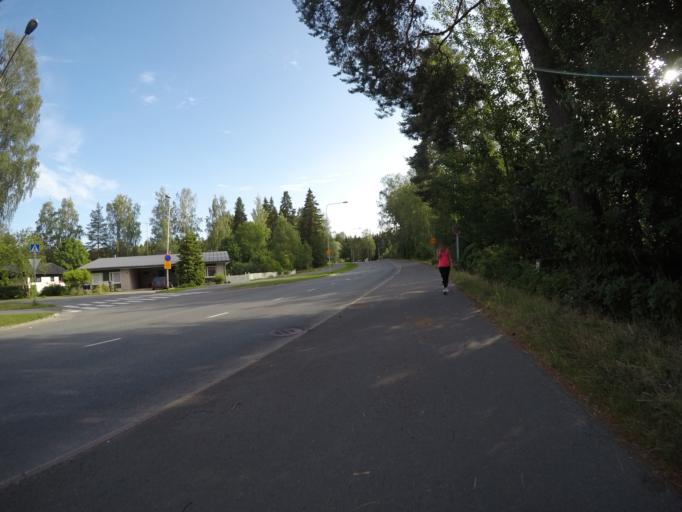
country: FI
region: Haeme
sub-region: Haemeenlinna
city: Haemeenlinna
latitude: 60.9745
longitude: 24.3921
